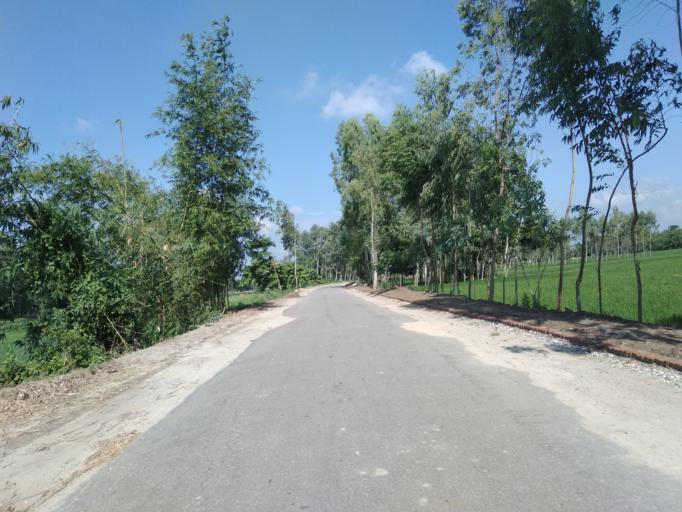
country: BD
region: Rangpur Division
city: Panchagarh
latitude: 26.2555
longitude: 88.6192
